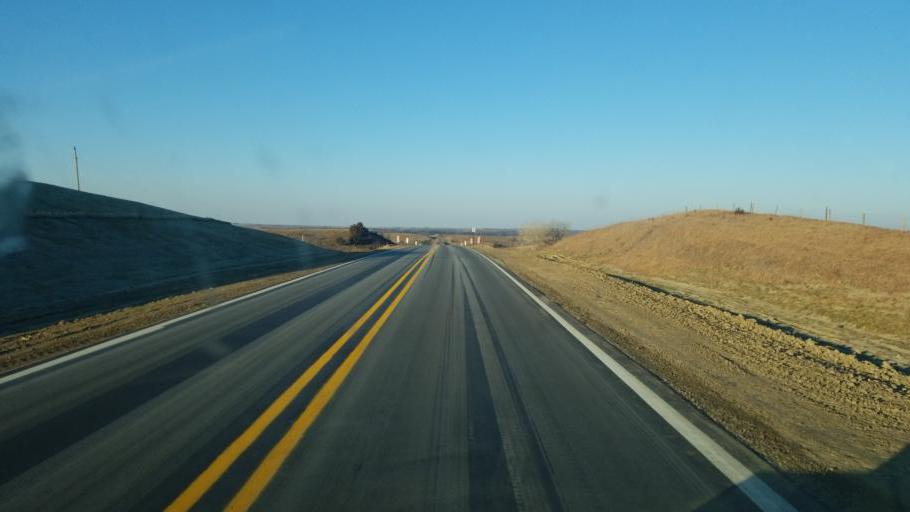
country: US
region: Nebraska
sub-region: Knox County
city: Center
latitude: 42.5972
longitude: -97.8349
